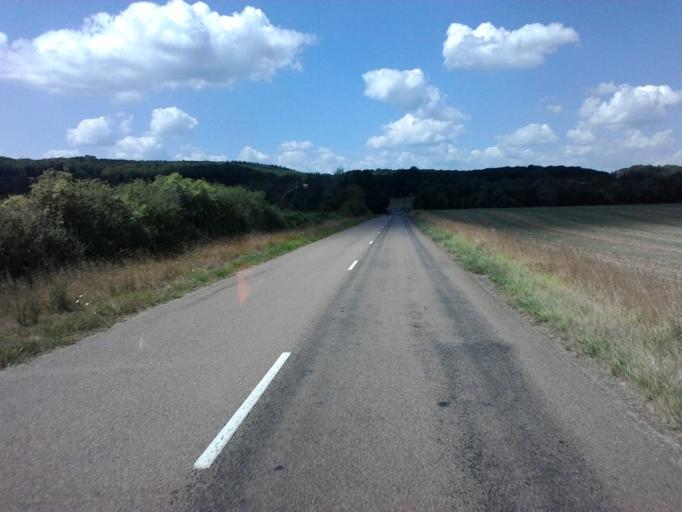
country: FR
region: Franche-Comte
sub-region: Departement du Jura
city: Montmorot
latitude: 46.7661
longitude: 5.5586
